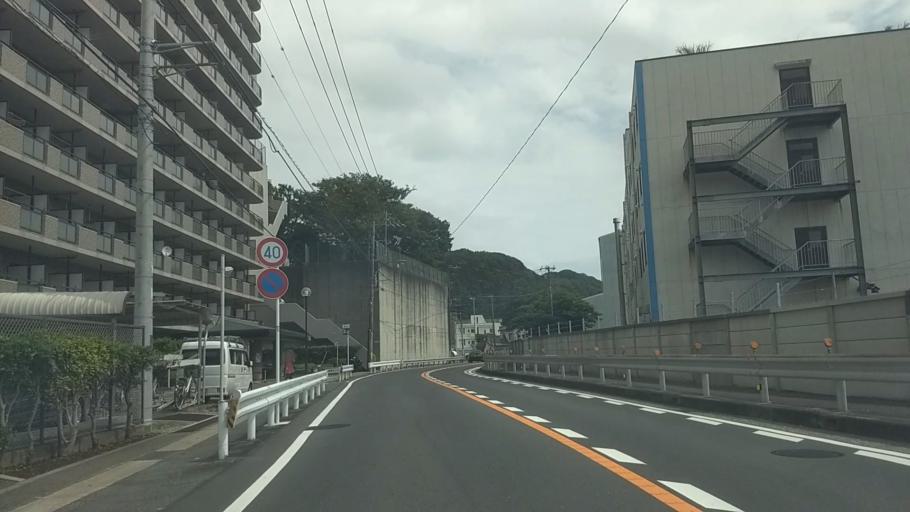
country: JP
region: Kanagawa
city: Yokosuka
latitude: 35.2463
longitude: 139.7191
